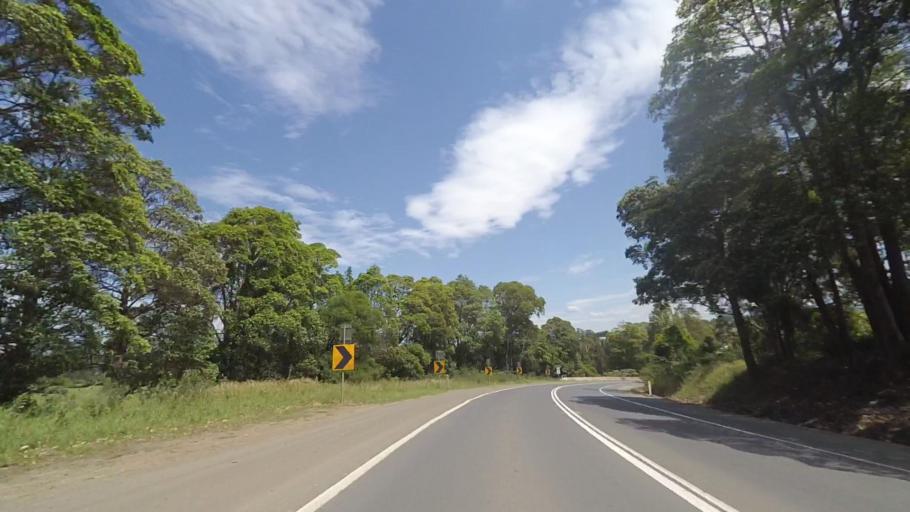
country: AU
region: New South Wales
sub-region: Shoalhaven Shire
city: Berry
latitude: -34.7606
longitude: 150.7394
